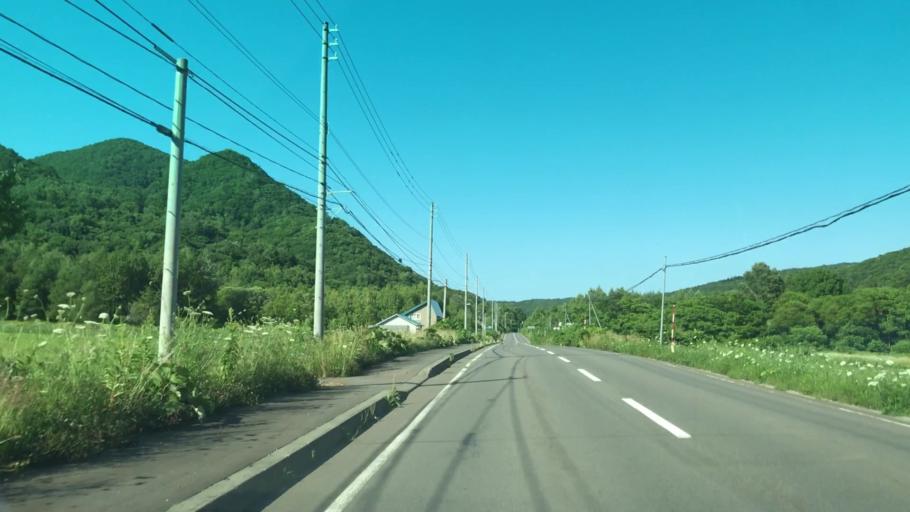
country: JP
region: Hokkaido
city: Yoichi
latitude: 43.0553
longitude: 140.8626
